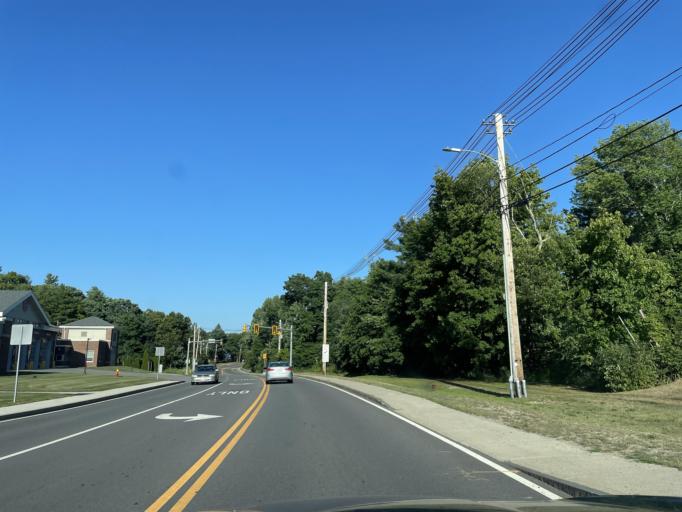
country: US
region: Massachusetts
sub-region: Bristol County
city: Mansfield
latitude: 42.0324
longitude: -71.1964
